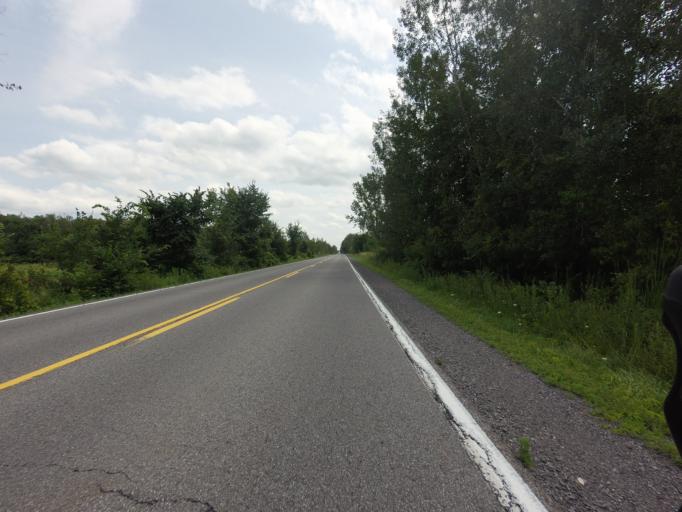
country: CA
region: Ontario
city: Ottawa
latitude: 45.2128
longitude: -75.5986
